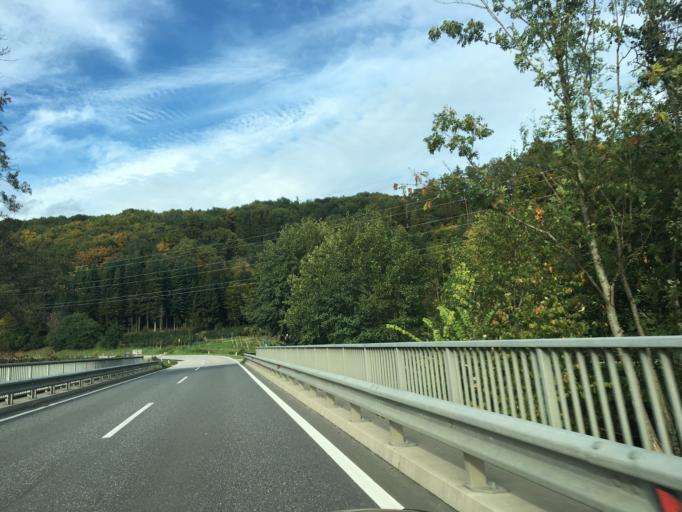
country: AT
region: Upper Austria
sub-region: Politischer Bezirk Urfahr-Umgebung
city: Feldkirchen an der Donau
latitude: 48.3625
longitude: 14.0677
